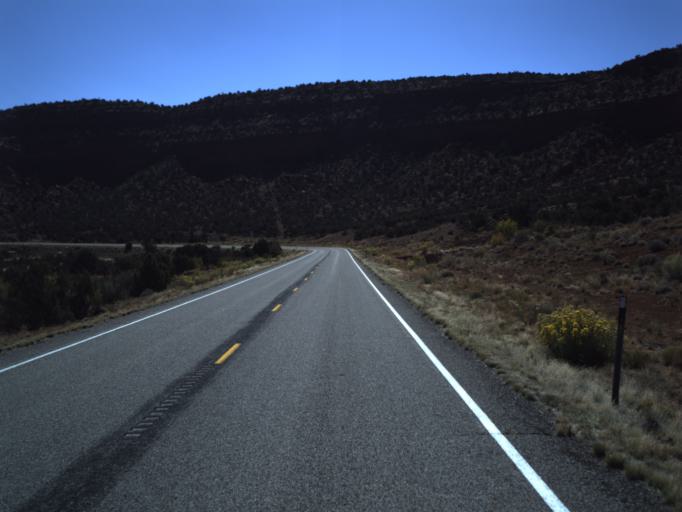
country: US
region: Utah
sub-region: San Juan County
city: Blanding
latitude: 37.6074
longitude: -110.0797
